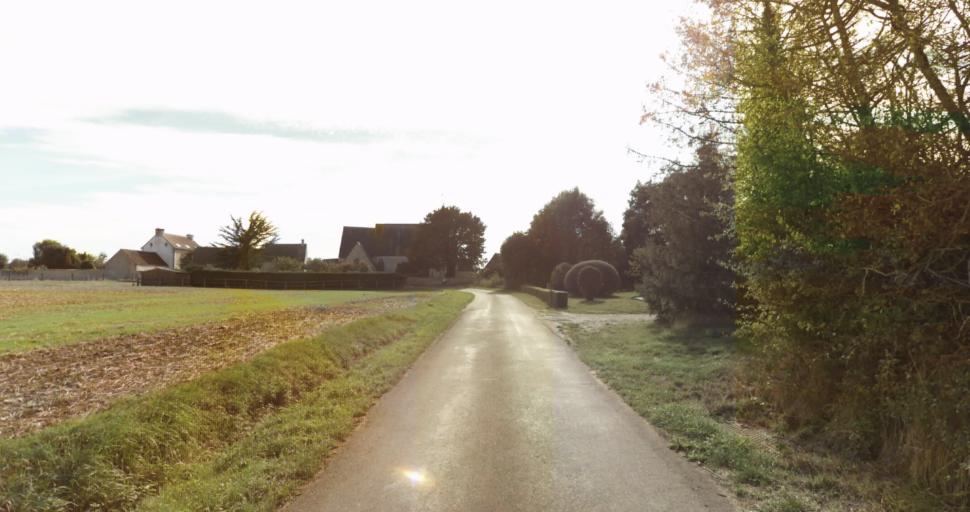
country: FR
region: Lower Normandy
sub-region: Departement de l'Orne
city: Gace
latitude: 48.7143
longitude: 0.2393
